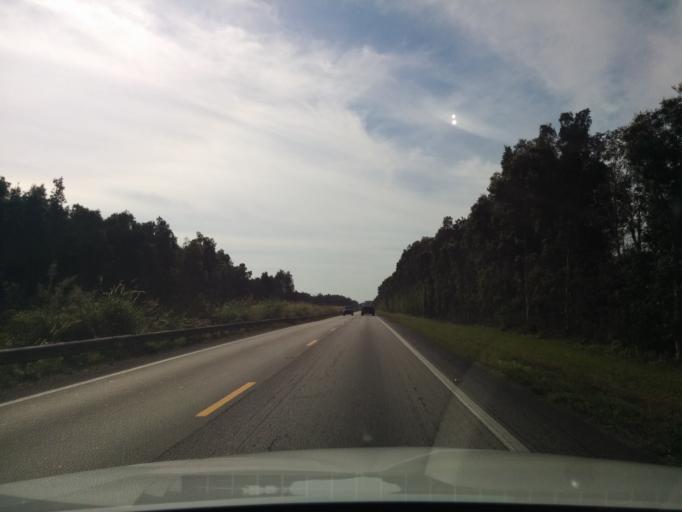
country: US
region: Florida
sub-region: Miami-Dade County
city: Kendall West
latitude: 25.7427
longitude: -80.4807
